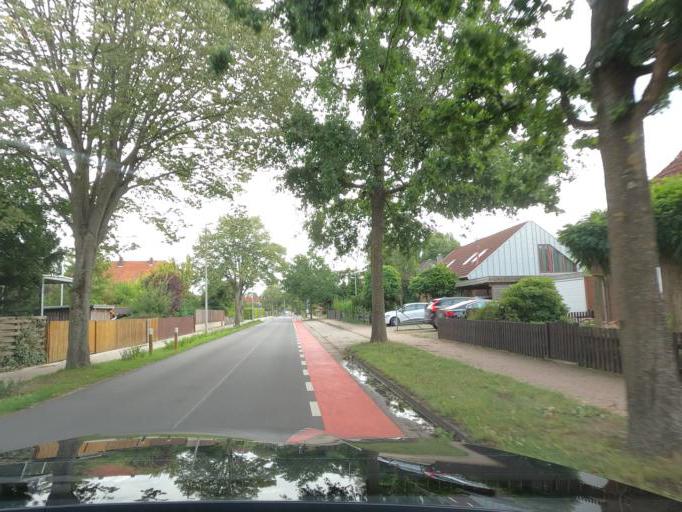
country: DE
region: Lower Saxony
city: Isernhagen Farster Bauerschaft
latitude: 52.5132
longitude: 9.9114
